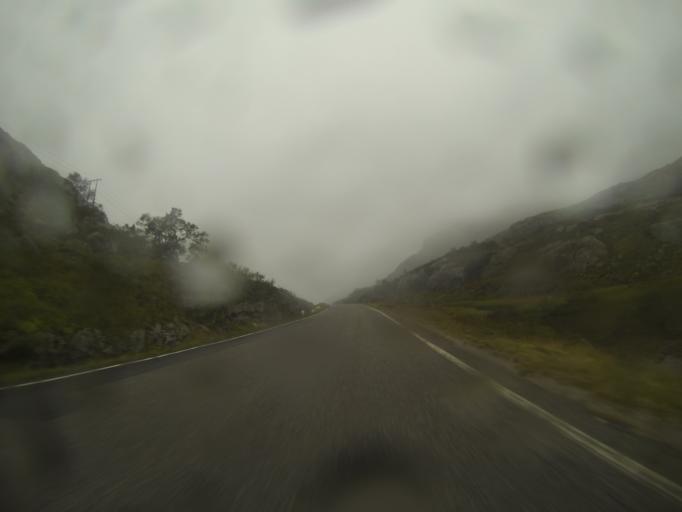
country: NO
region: Vest-Agder
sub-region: Sirdal
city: Tonstad
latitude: 58.9079
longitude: 6.7187
